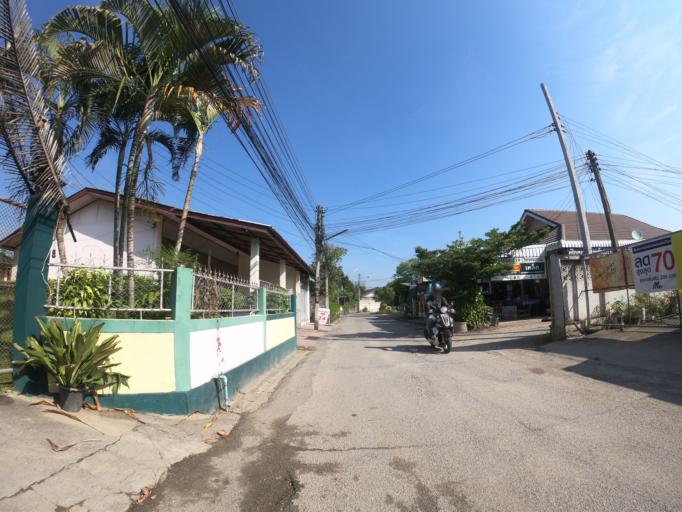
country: TH
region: Chiang Mai
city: Chiang Mai
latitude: 18.7439
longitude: 98.9870
